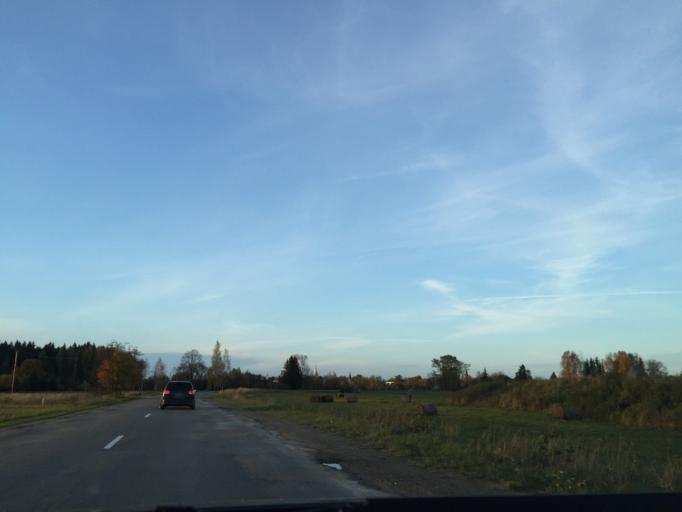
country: LV
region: Malpils
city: Malpils
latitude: 56.8947
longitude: 24.9296
